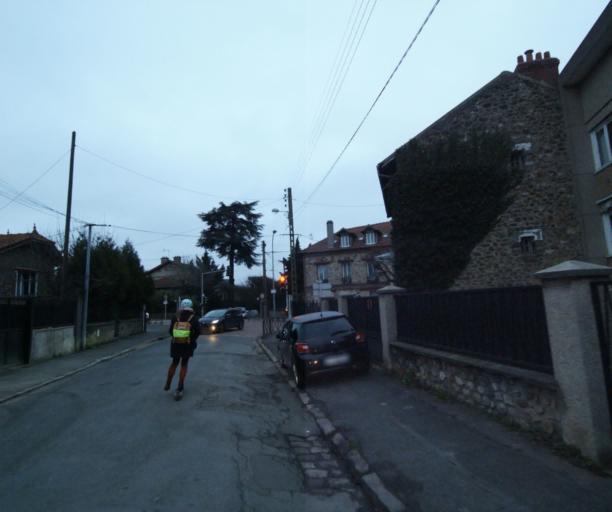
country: FR
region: Ile-de-France
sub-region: Departement du Val-de-Marne
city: Villeneuve-le-Roi
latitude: 48.7313
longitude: 2.4134
